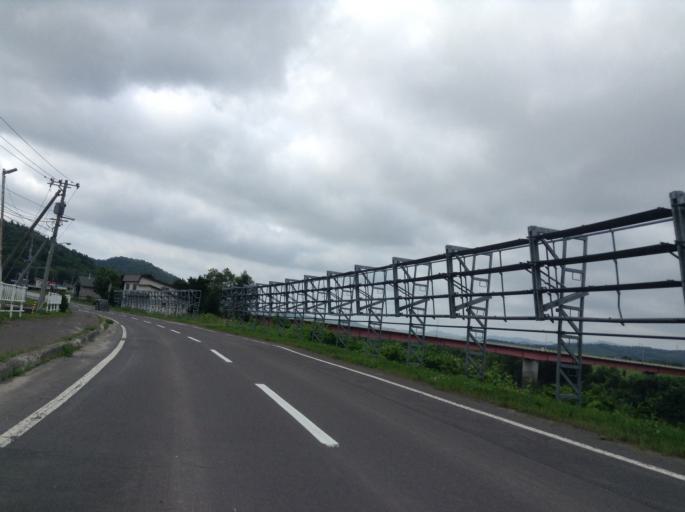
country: JP
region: Hokkaido
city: Nayoro
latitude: 44.8056
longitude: 142.0718
